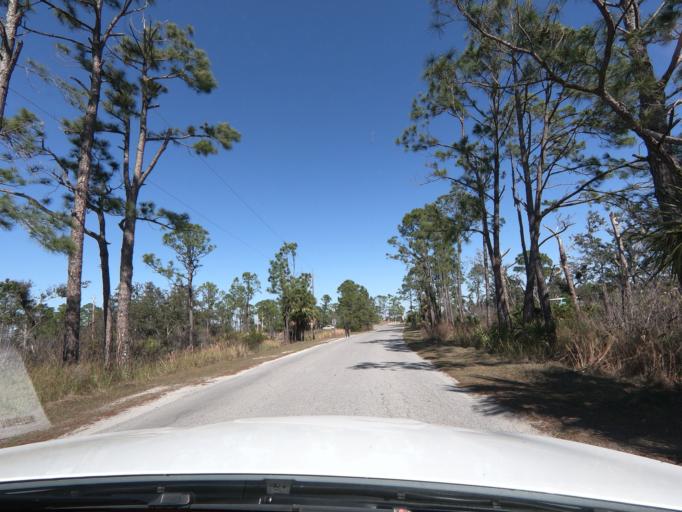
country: US
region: Florida
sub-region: Bay County
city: Lower Grand Lagoon
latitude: 30.1300
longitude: -85.7331
